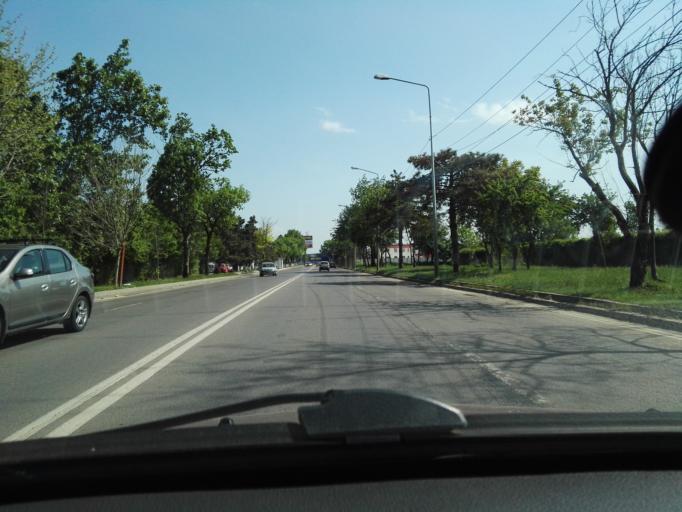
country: RO
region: Ilfov
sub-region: Comuna Popesti-Leordeni
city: Popesti-Leordeni
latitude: 44.3675
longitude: 26.1247
